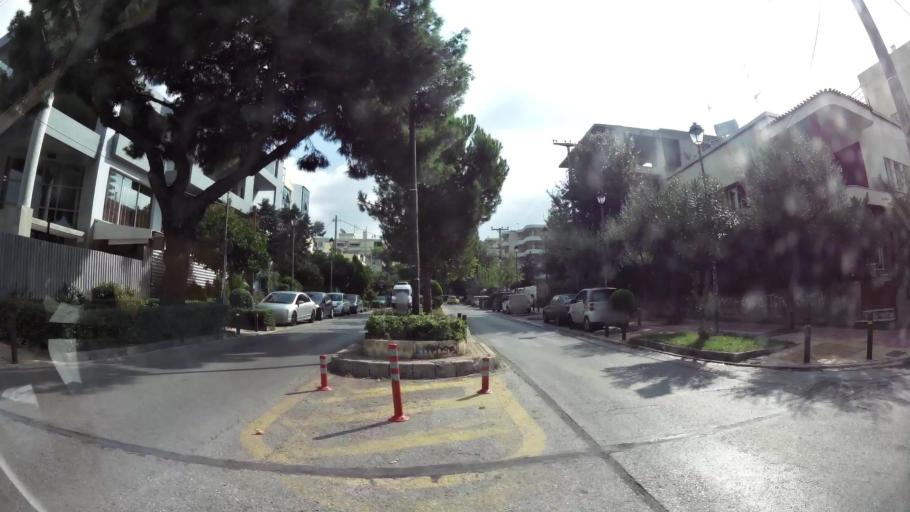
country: GR
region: Attica
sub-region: Nomarchia Athinas
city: Cholargos
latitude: 37.9998
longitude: 23.7978
